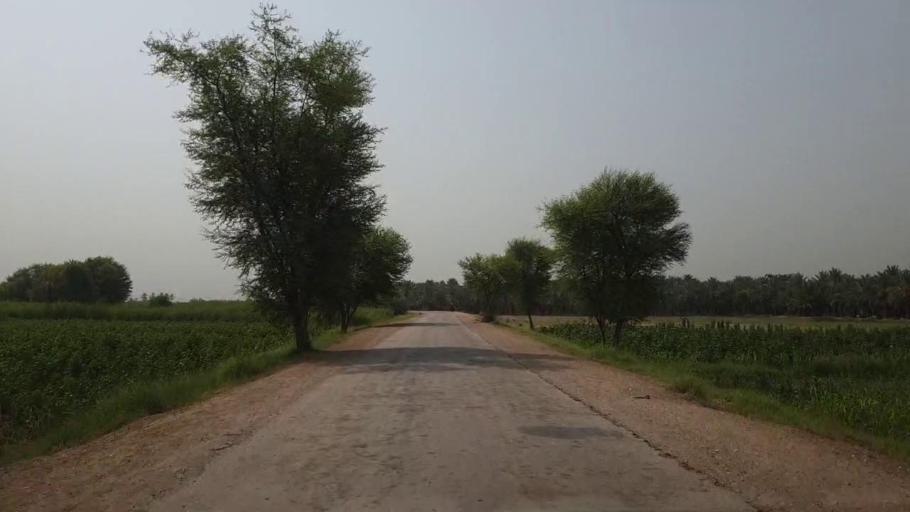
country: PK
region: Sindh
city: Gambat
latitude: 27.4310
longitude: 68.5343
